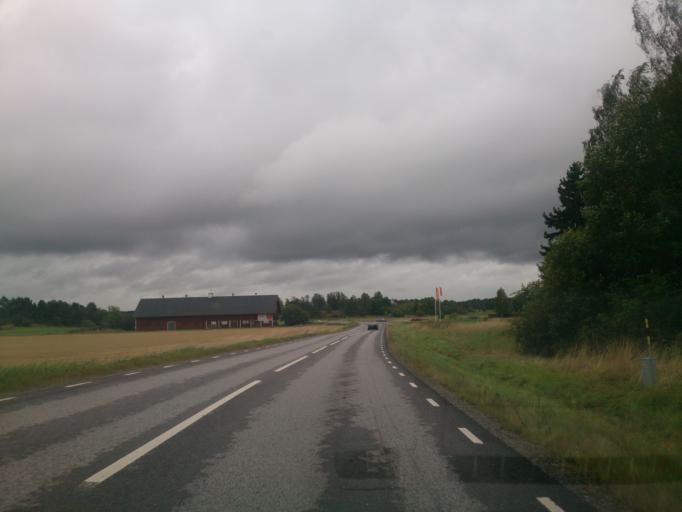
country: SE
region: OEstergoetland
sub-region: Norrkopings Kommun
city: Krokek
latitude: 58.5797
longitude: 16.5680
